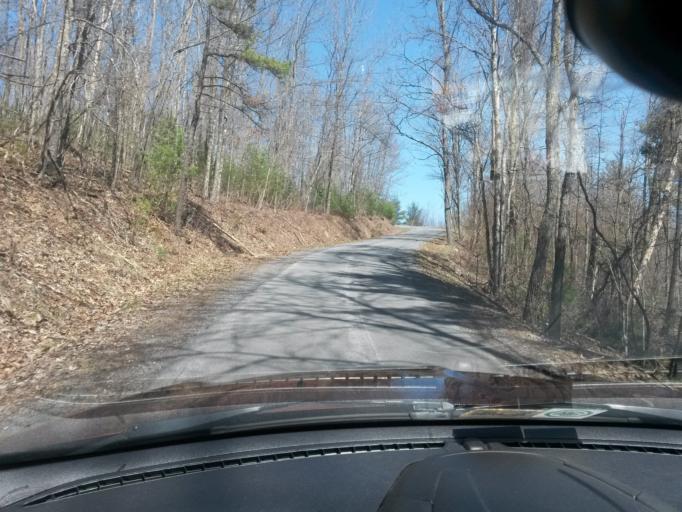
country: US
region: West Virginia
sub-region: Greenbrier County
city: White Sulphur Springs
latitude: 37.6741
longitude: -80.3196
